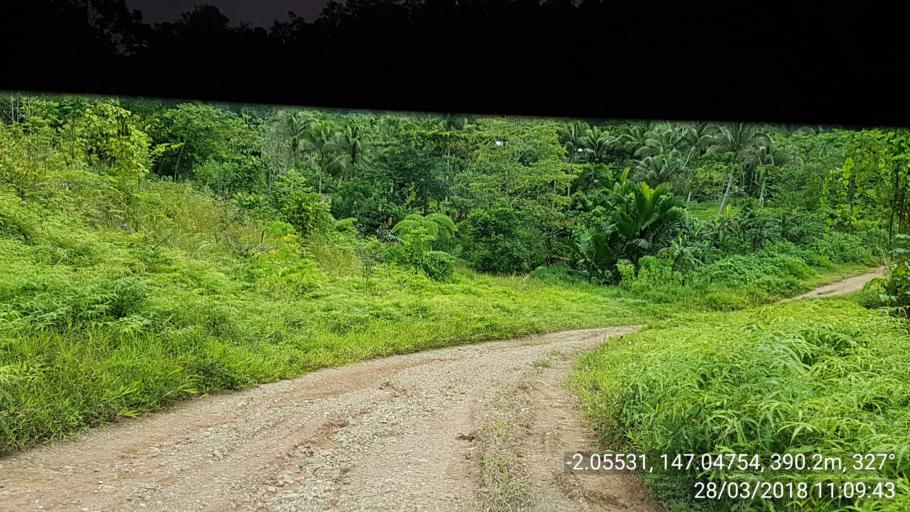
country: PG
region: Manus
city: Lorengau
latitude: -2.0553
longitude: 147.0475
